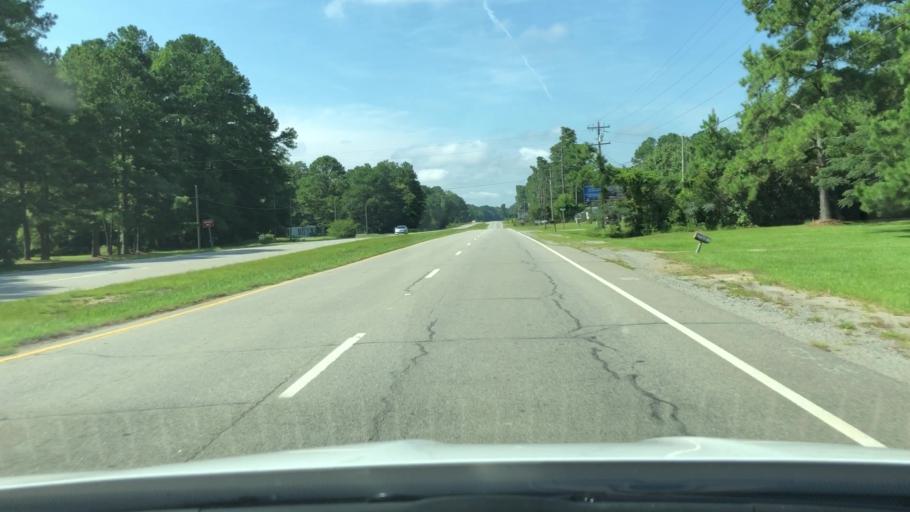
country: US
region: North Carolina
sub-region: Bertie County
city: Windsor
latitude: 35.9570
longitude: -76.9538
